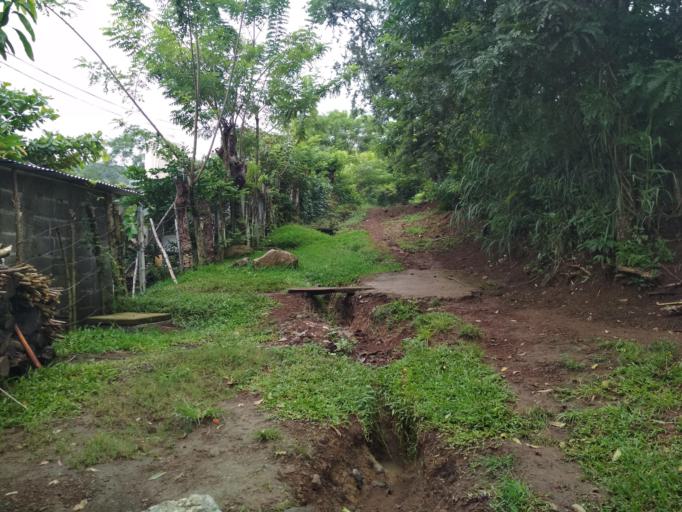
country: MX
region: Veracruz
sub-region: San Andres Tuxtla
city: Cerro las Iguanas
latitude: 18.4134
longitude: -95.2004
